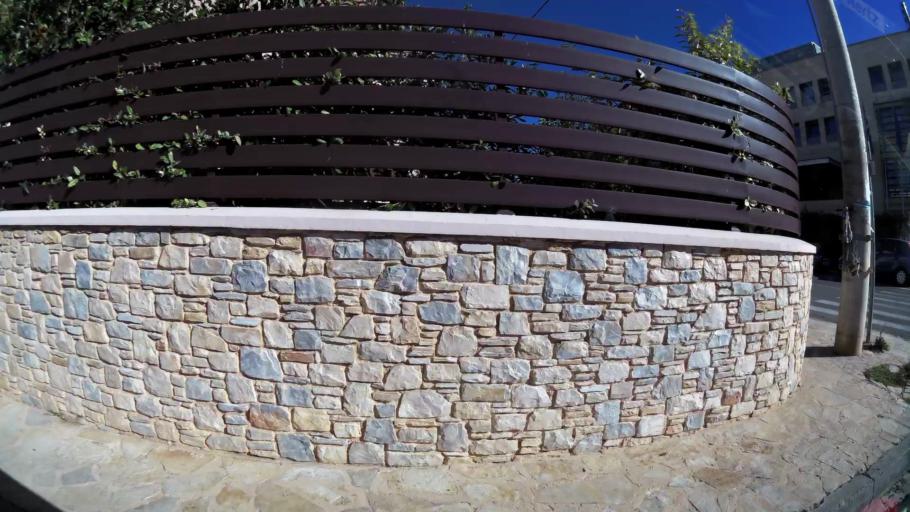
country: GR
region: Attica
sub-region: Nomarchia Anatolikis Attikis
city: Gerakas
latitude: 38.0202
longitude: 23.8549
